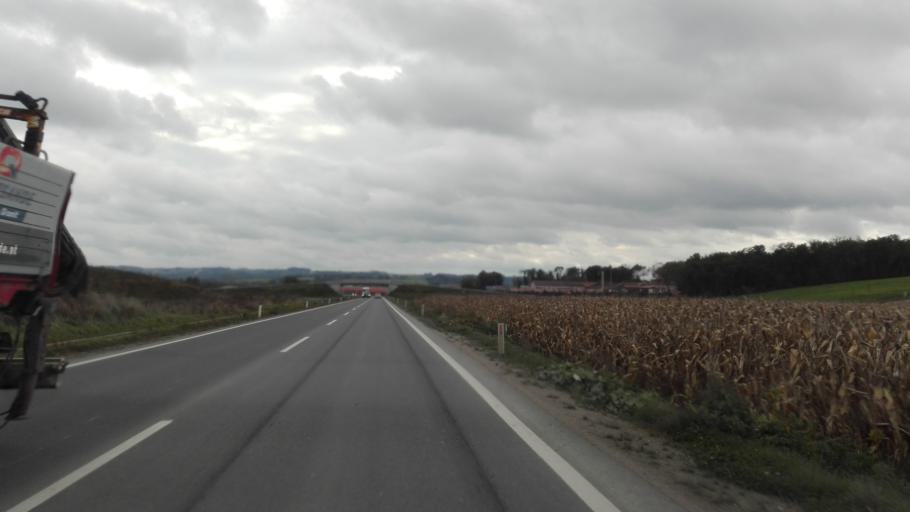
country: AT
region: Upper Austria
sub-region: Politischer Bezirk Urfahr-Umgebung
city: Feldkirchen an der Donau
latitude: 48.3042
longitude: 14.0026
